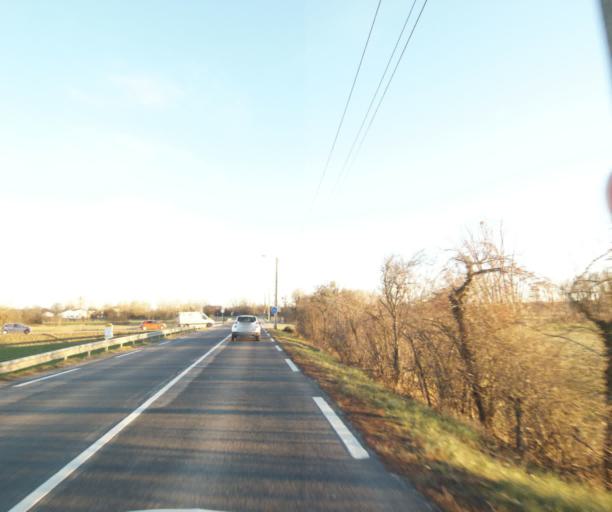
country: FR
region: Lorraine
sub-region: Departement de Meurthe-et-Moselle
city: Laneuveville-devant-Nancy
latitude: 48.6637
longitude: 6.2371
